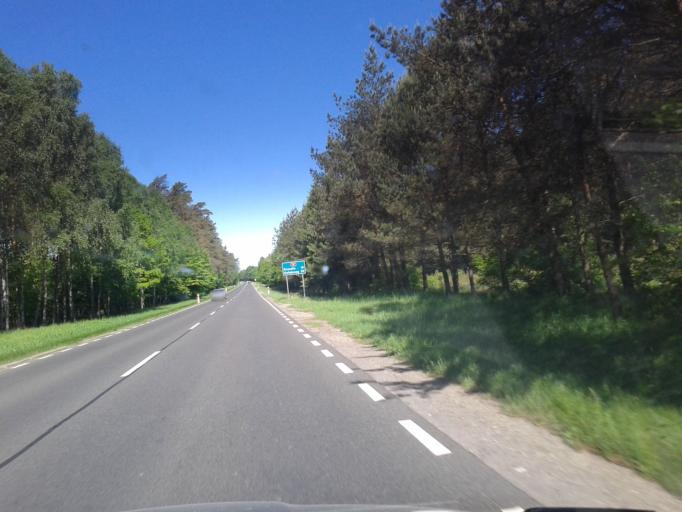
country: PL
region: West Pomeranian Voivodeship
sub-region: Powiat koszalinski
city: Sianow
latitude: 54.0792
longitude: 16.3902
